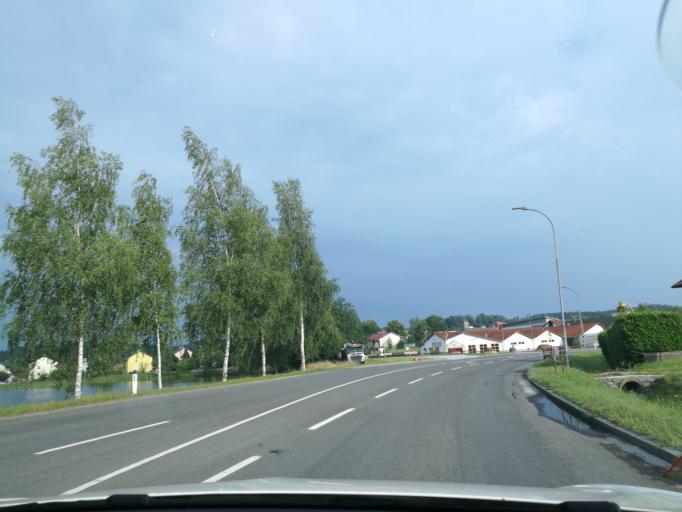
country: AT
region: Lower Austria
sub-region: Politischer Bezirk Gmund
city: Heidenreichstein
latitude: 48.8707
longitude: 15.1216
